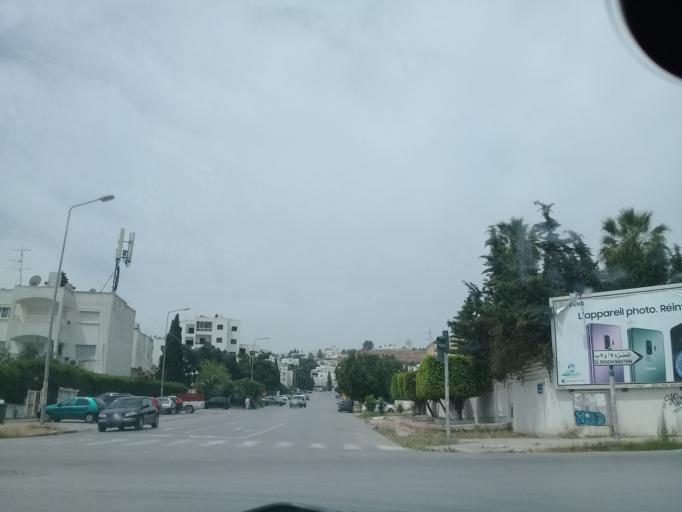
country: TN
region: Tunis
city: Tunis
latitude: 36.8415
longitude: 10.1555
